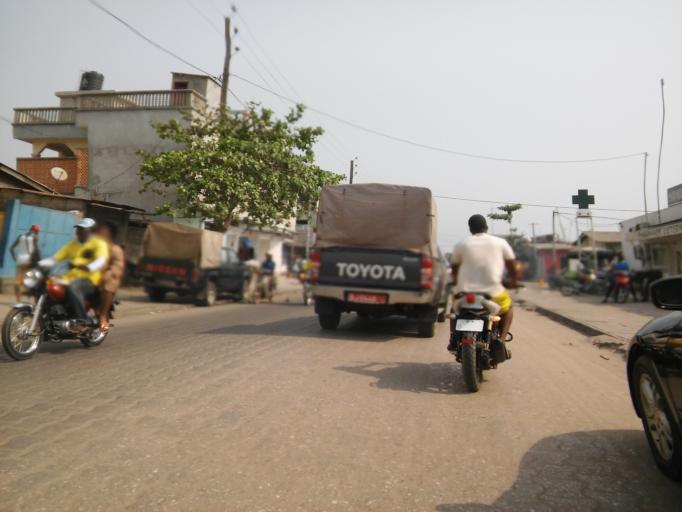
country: BJ
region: Littoral
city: Cotonou
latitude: 6.3779
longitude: 2.4113
